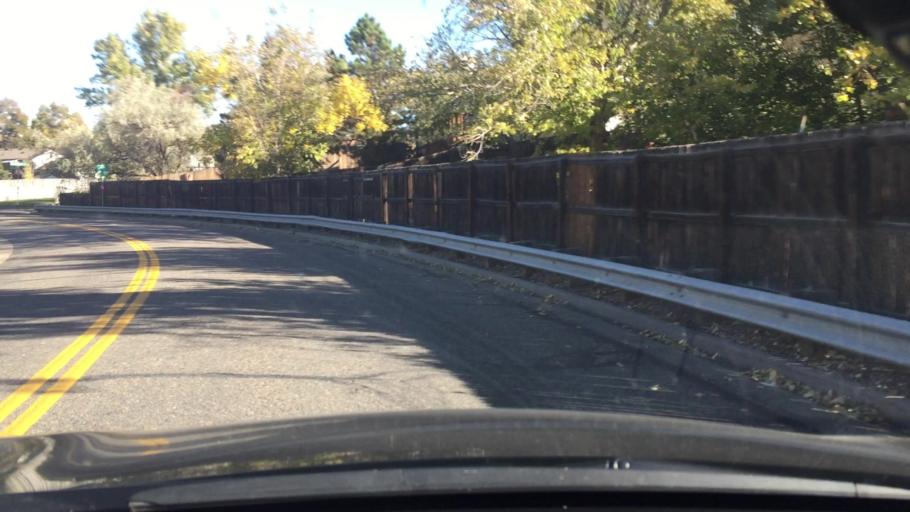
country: US
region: Colorado
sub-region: Arapahoe County
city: Dove Valley
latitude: 39.6298
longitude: -104.7941
